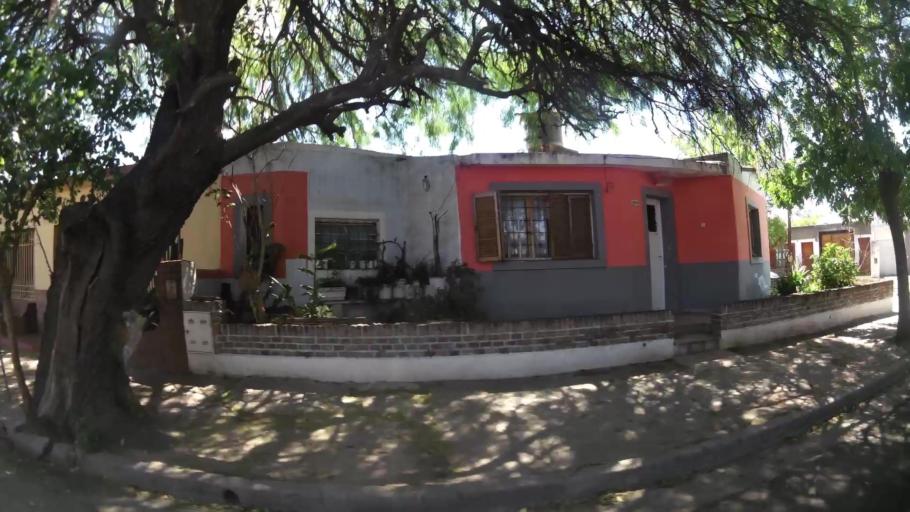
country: AR
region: Cordoba
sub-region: Departamento de Capital
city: Cordoba
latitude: -31.3772
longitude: -64.1617
